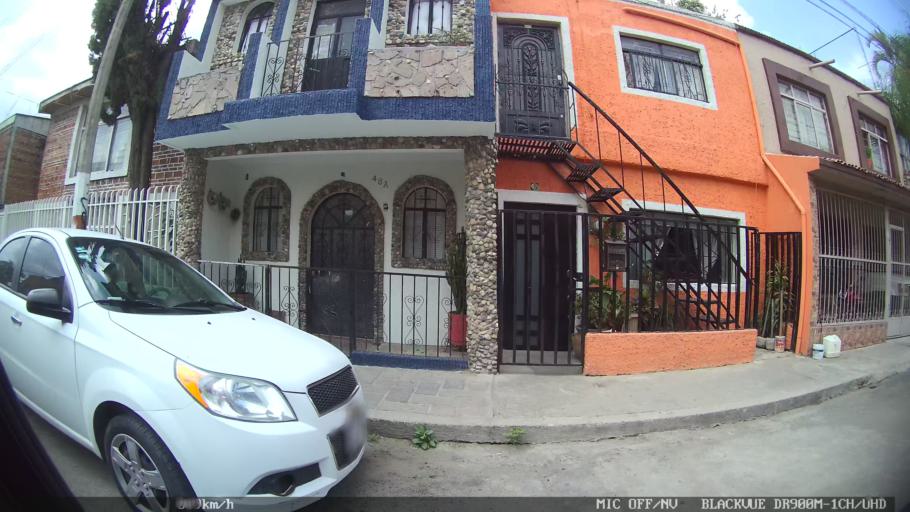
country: MX
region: Jalisco
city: Tonala
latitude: 20.6181
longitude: -103.2426
